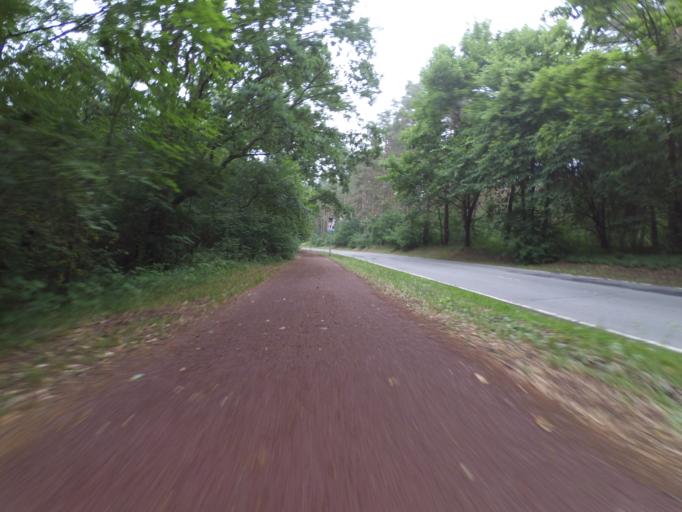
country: DE
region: Mecklenburg-Vorpommern
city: Plau am See
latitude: 53.4754
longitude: 12.2818
